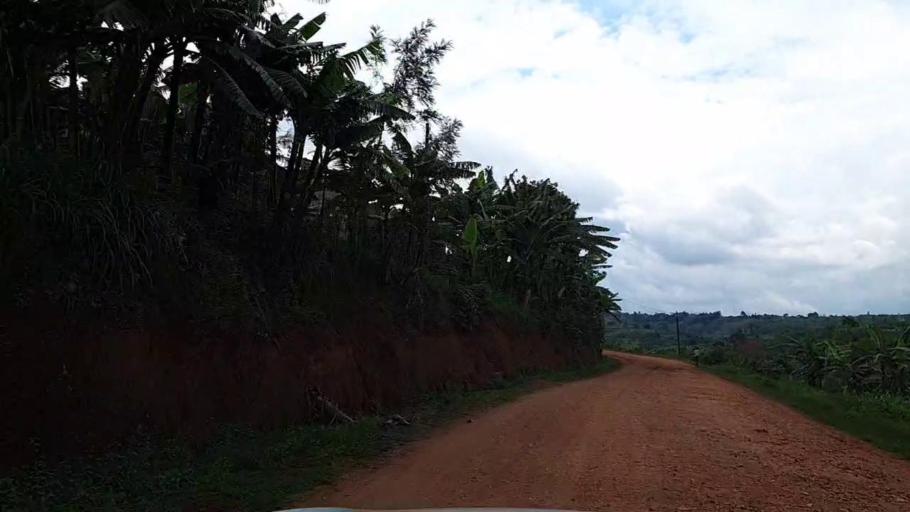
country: RW
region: Southern Province
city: Nyanza
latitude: -2.4152
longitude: 29.6691
